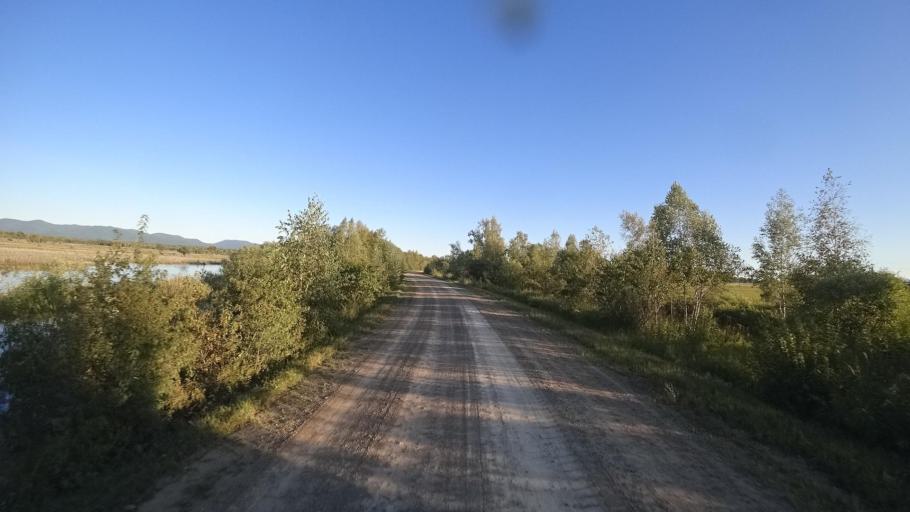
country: RU
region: Primorskiy
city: Kirovskiy
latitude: 44.7874
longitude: 133.6229
